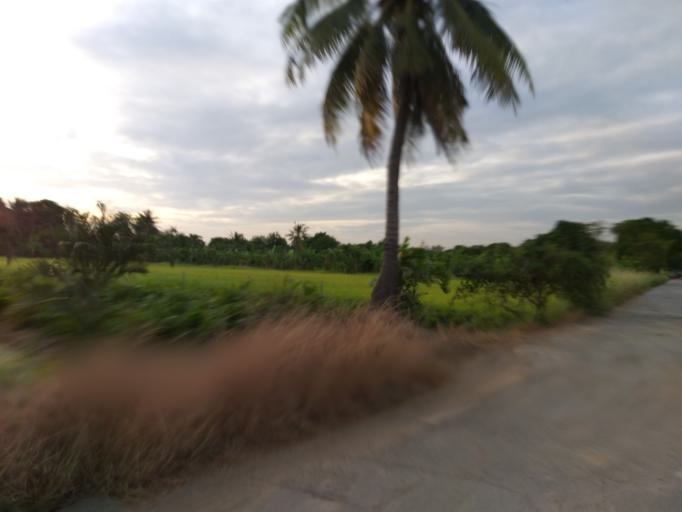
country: TH
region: Pathum Thani
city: Ban Lam Luk Ka
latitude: 13.9977
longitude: 100.7999
